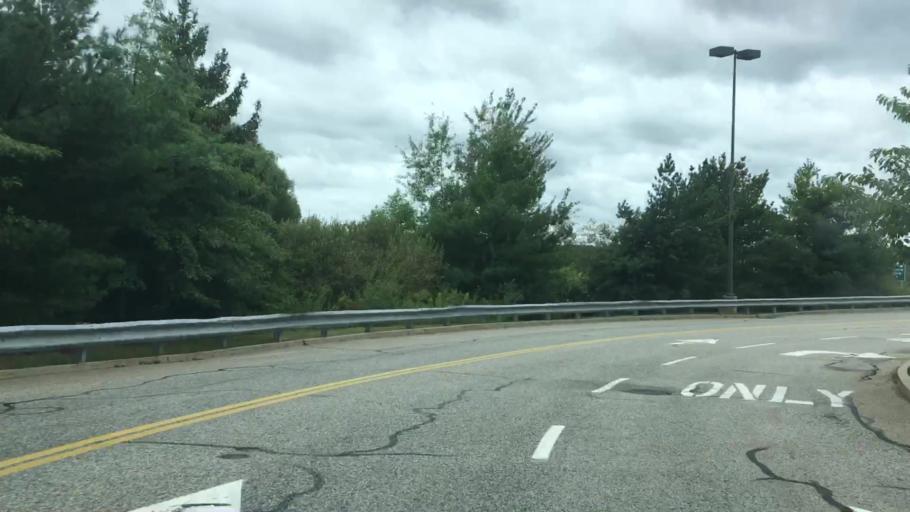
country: US
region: Maine
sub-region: Cumberland County
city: South Portland Gardens
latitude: 43.6356
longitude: -70.3436
